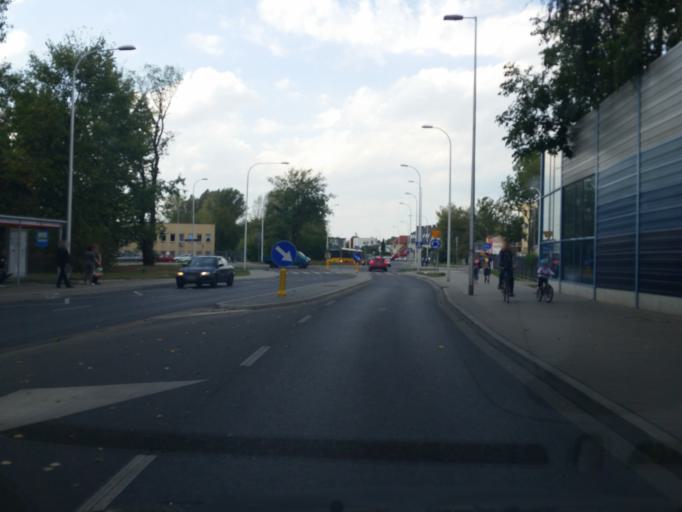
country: PL
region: Masovian Voivodeship
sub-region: Warszawa
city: Wlochy
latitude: 52.1965
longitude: 20.9252
